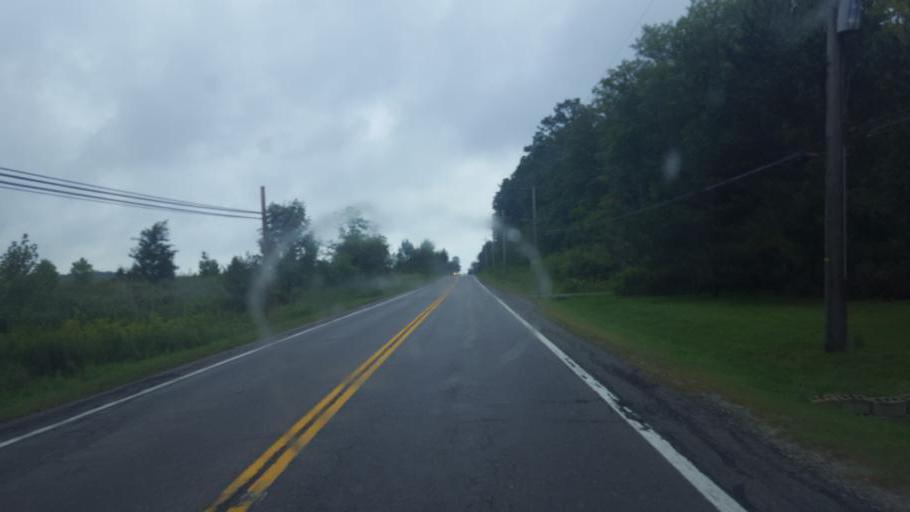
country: US
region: Ohio
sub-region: Geauga County
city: Burton
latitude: 41.5382
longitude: -81.1941
